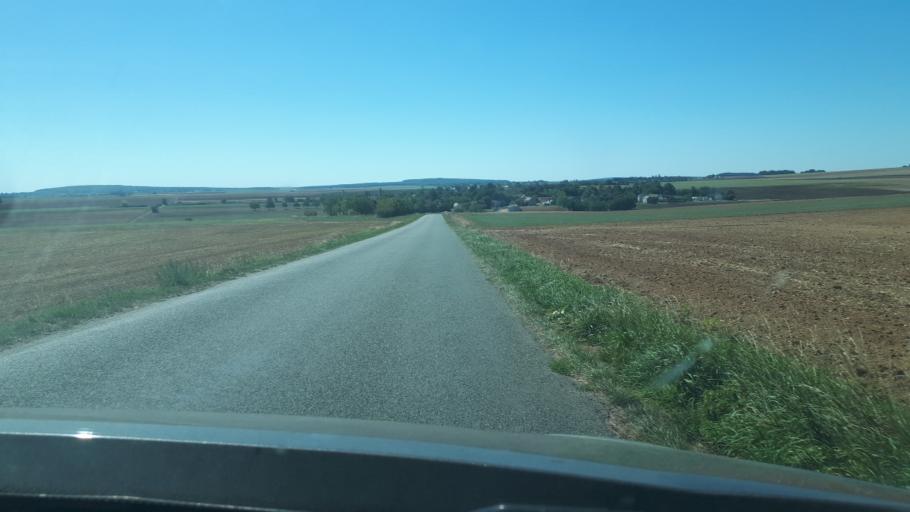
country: FR
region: Centre
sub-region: Departement du Cher
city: Baugy
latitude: 47.2157
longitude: 2.7494
